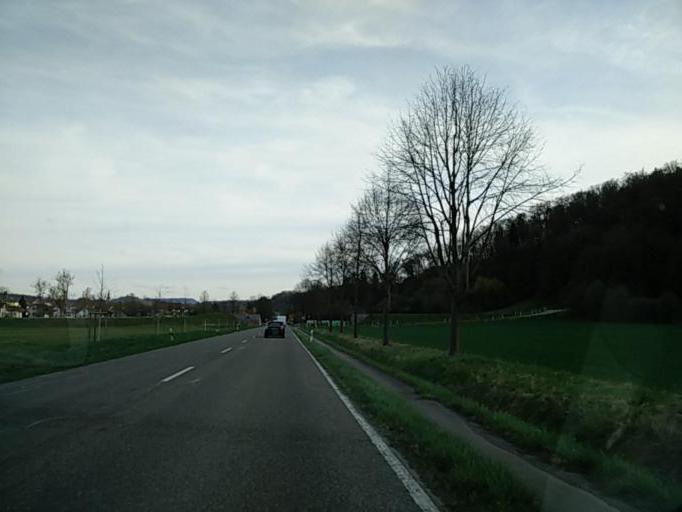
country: DE
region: Baden-Wuerttemberg
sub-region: Tuebingen Region
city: Tuebingen
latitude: 48.5376
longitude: 9.0768
